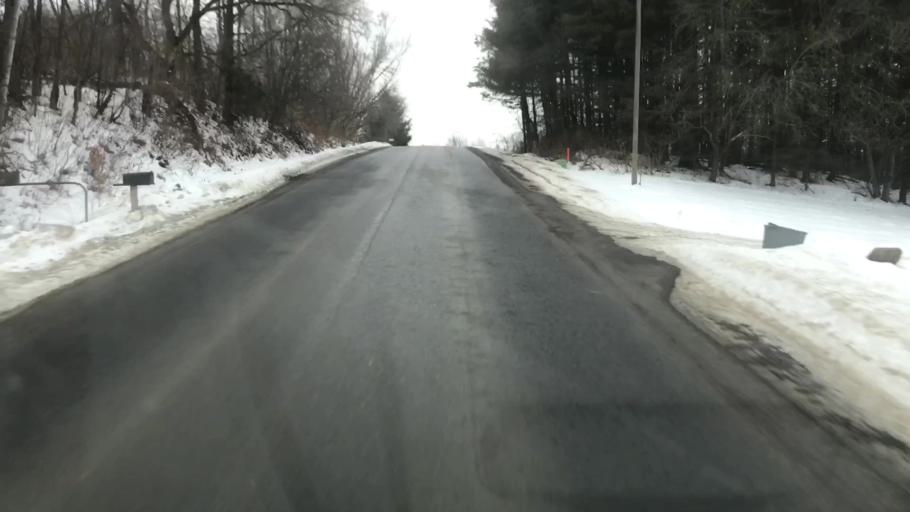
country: US
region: New York
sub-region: Cortland County
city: Cortland West
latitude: 42.6692
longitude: -76.2765
